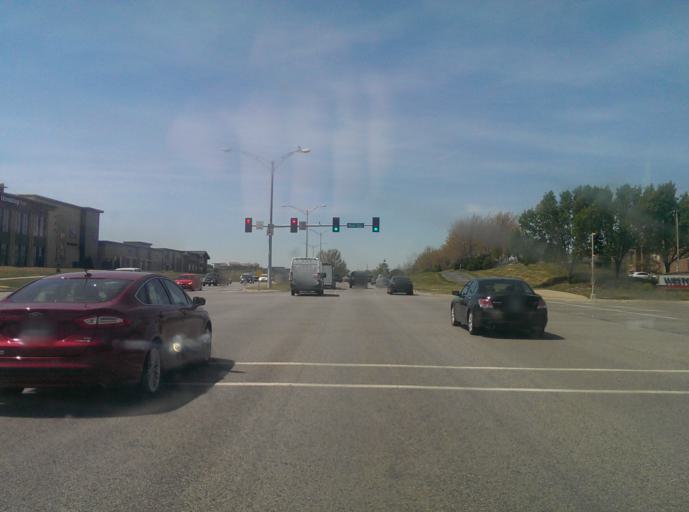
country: US
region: Kansas
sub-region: Johnson County
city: Leawood
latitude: 38.8838
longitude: -94.6490
